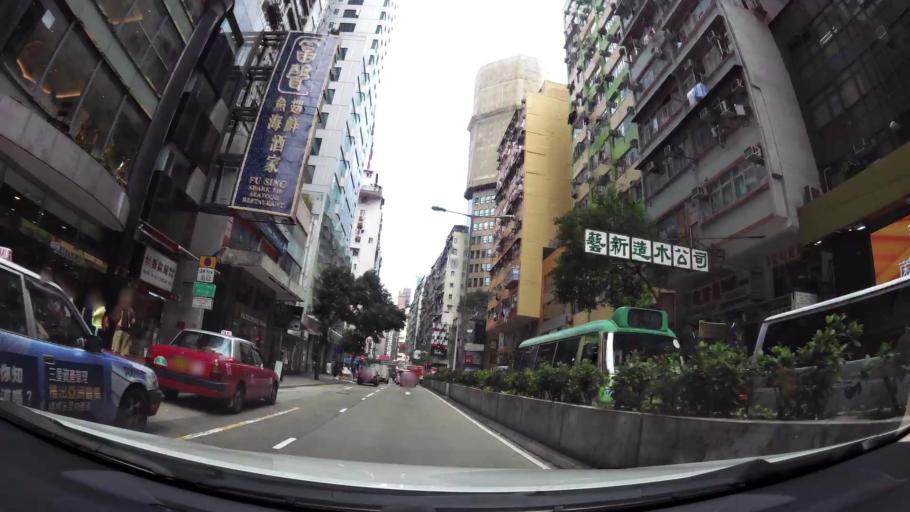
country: HK
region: Wanchai
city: Wan Chai
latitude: 22.2794
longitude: 114.1790
